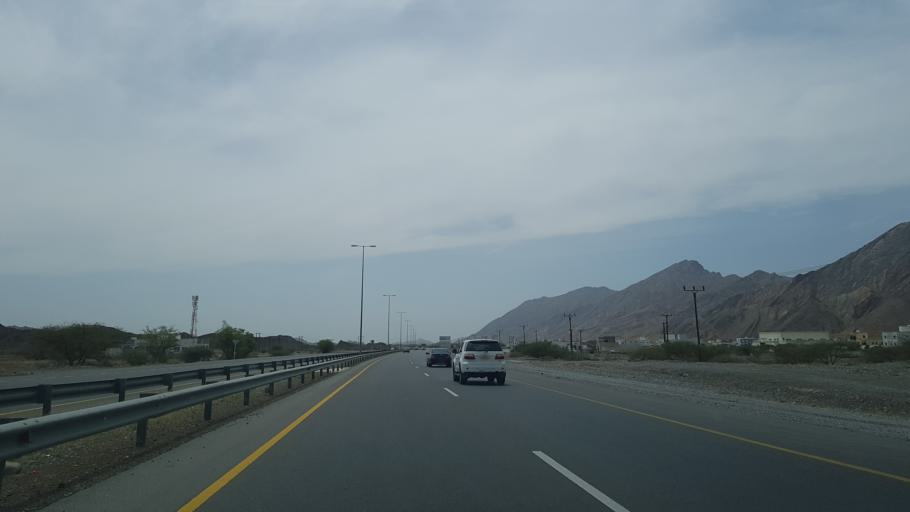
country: OM
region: Muhafazat ad Dakhiliyah
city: Izki
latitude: 23.0329
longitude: 57.7989
